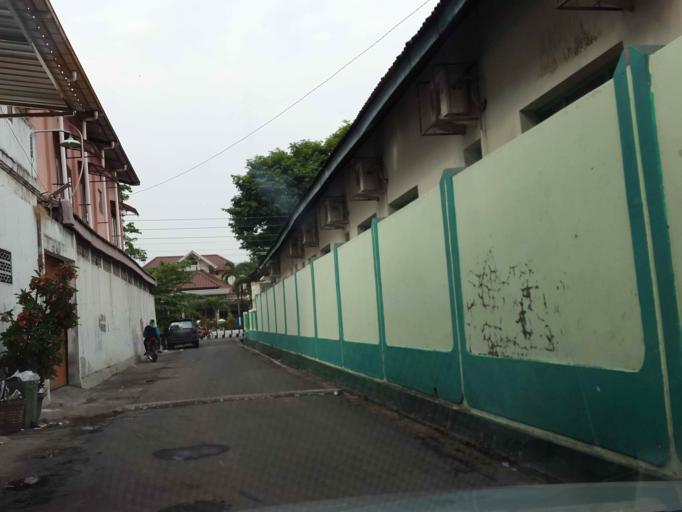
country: ID
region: Central Java
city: Jaten
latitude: -7.5989
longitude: 110.9560
